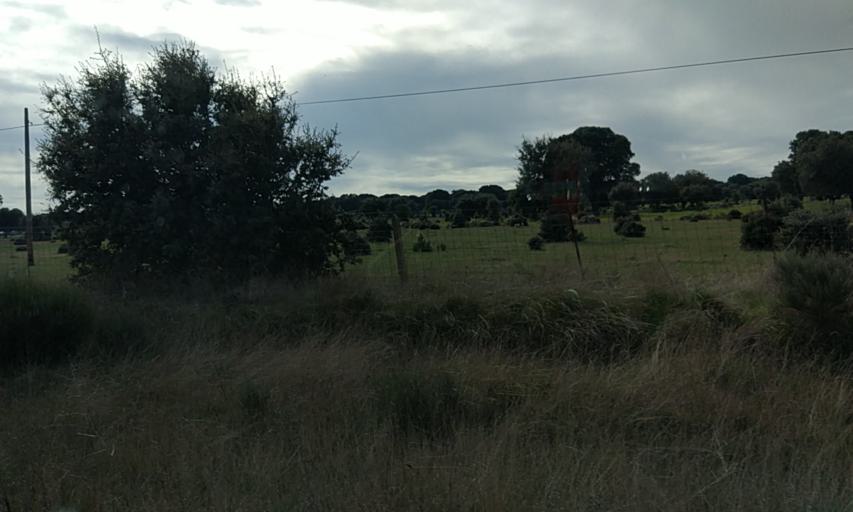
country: ES
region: Castille and Leon
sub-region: Provincia de Salamanca
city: Herguijuela de Ciudad Rodrigo
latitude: 40.4646
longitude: -6.5861
